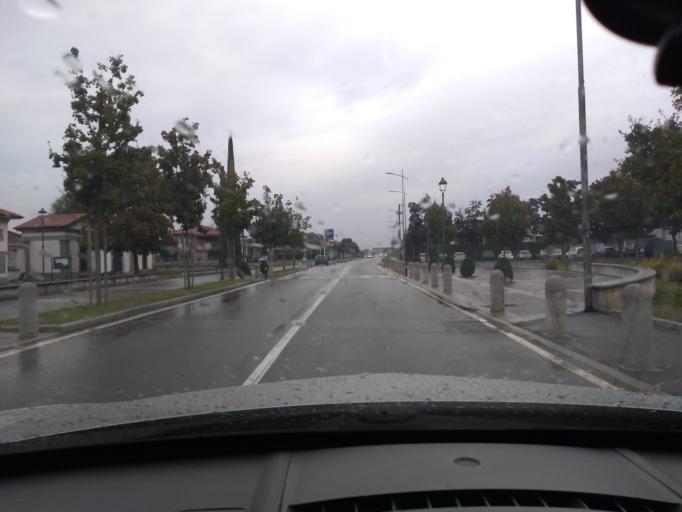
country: IT
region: Lombardy
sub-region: Provincia di Bergamo
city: Mornico al Serio
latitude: 45.5978
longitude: 9.8088
